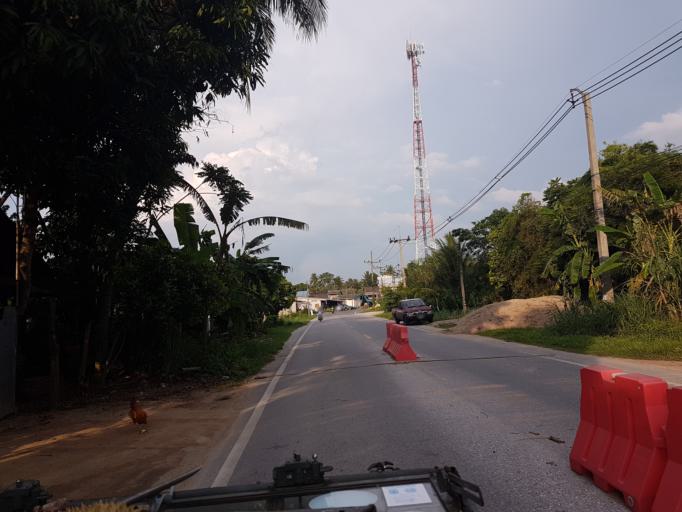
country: TH
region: Pattani
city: Khok Pho
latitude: 6.6753
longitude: 101.0998
